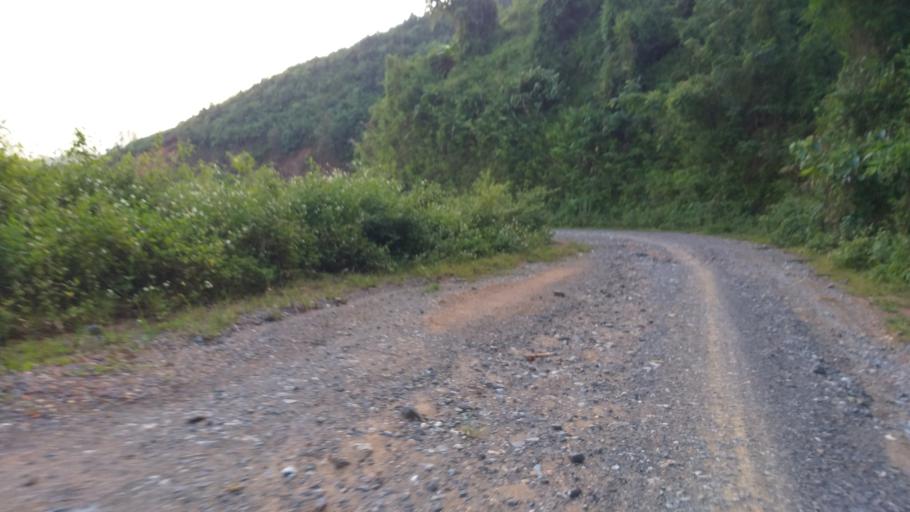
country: LA
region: Phongsali
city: Khoa
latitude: 21.1922
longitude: 102.5599
